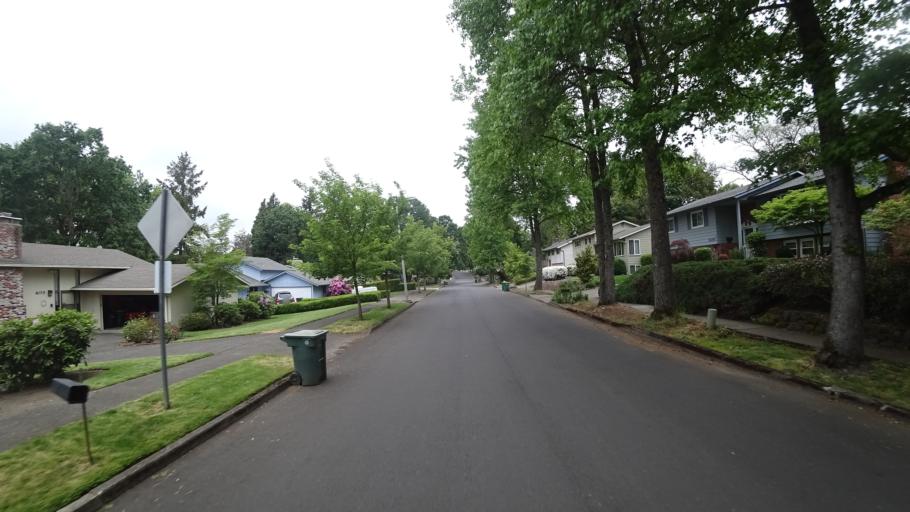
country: US
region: Oregon
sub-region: Washington County
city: Raleigh Hills
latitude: 45.4761
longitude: -122.7748
